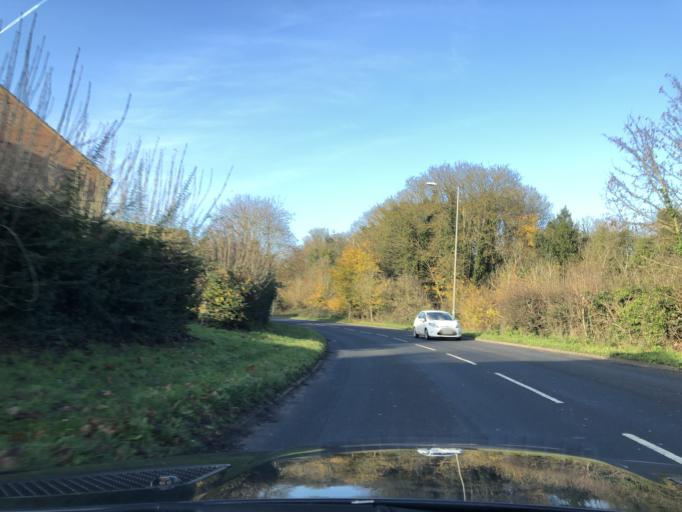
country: GB
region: England
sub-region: Buckinghamshire
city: Marlow
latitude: 51.5831
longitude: -0.7607
